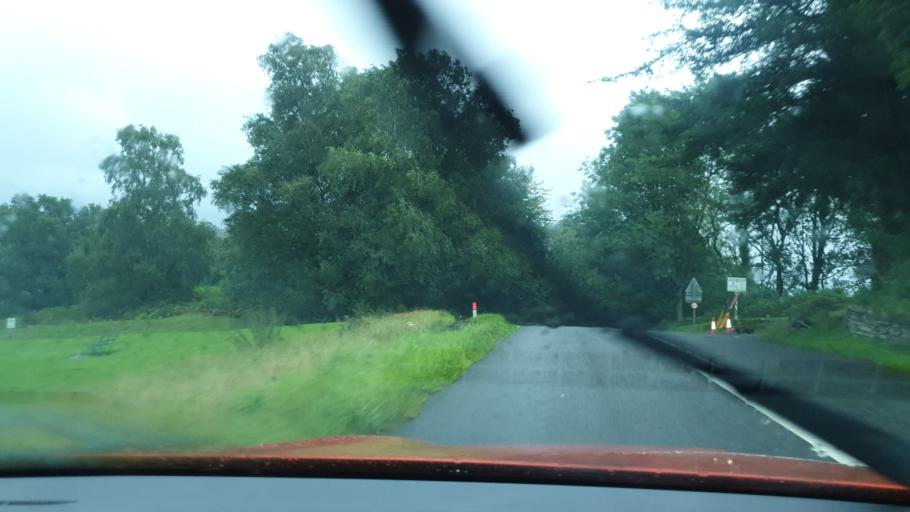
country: GB
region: England
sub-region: Cumbria
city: Ulverston
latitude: 54.2587
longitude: -3.0820
